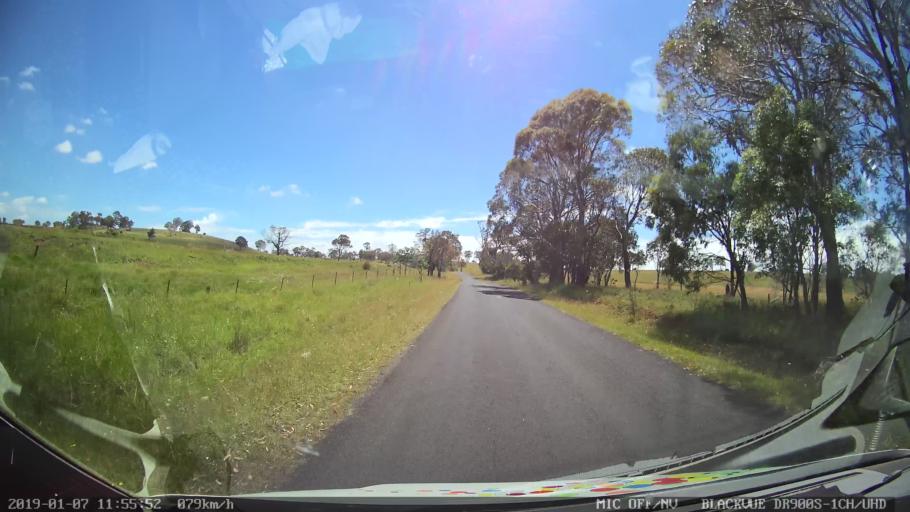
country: AU
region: New South Wales
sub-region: Guyra
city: Guyra
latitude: -30.2809
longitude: 151.6724
